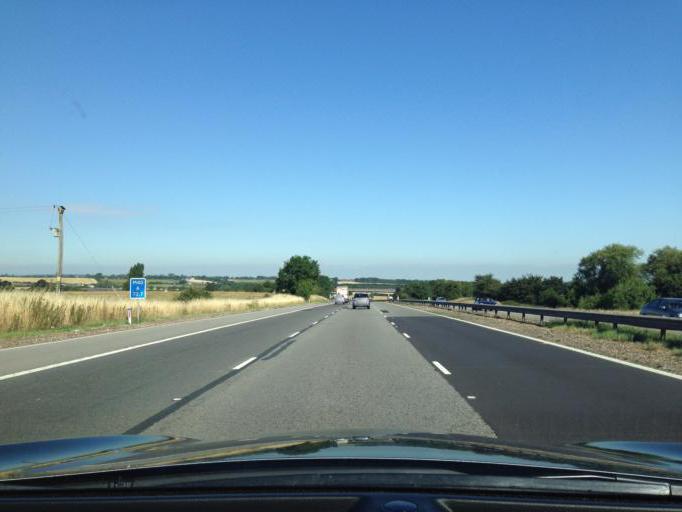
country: GB
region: England
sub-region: Oxfordshire
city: Thame
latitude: 51.7113
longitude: -1.0159
